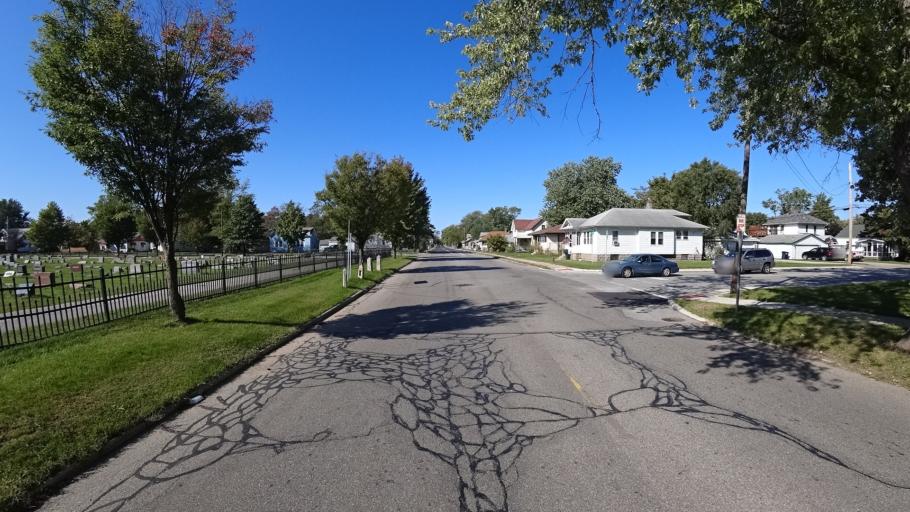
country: US
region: Indiana
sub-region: LaPorte County
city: Michigan City
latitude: 41.7059
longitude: -86.8859
